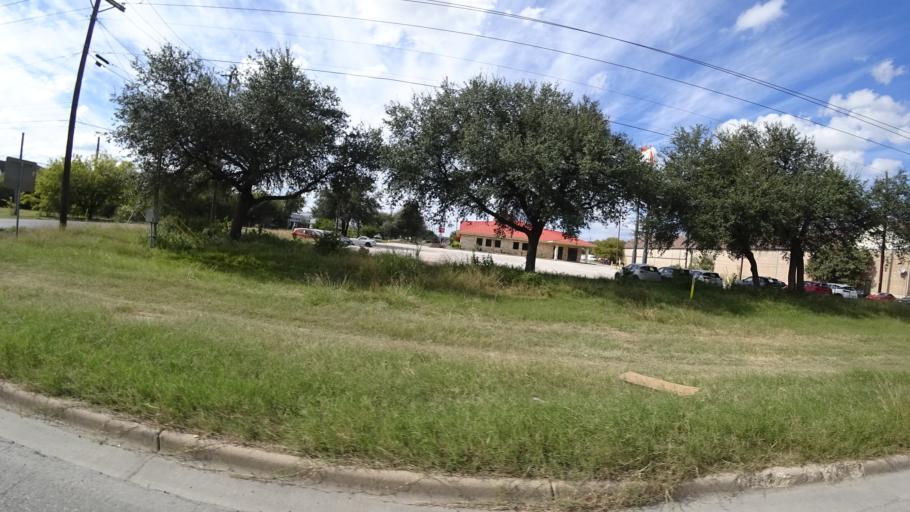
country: US
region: Texas
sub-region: Travis County
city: Austin
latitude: 30.2136
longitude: -97.7538
